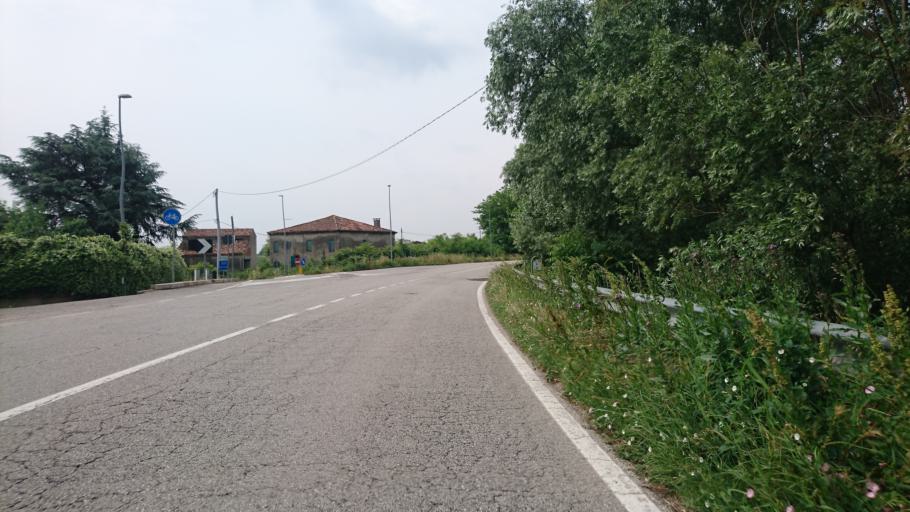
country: IT
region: Veneto
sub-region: Provincia di Padova
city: Vighizzolo d'Este
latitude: 45.1421
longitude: 11.6427
